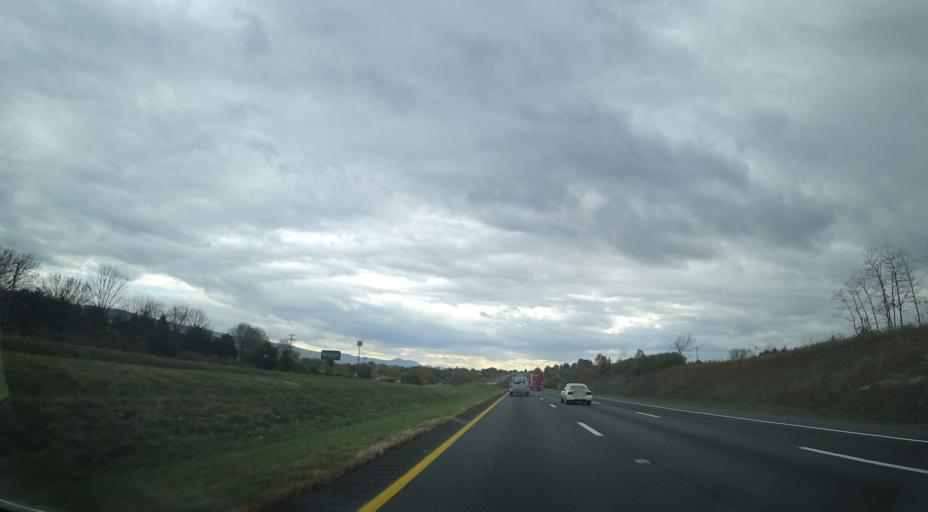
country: US
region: Virginia
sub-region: Shenandoah County
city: New Market
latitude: 38.6523
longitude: -78.6736
